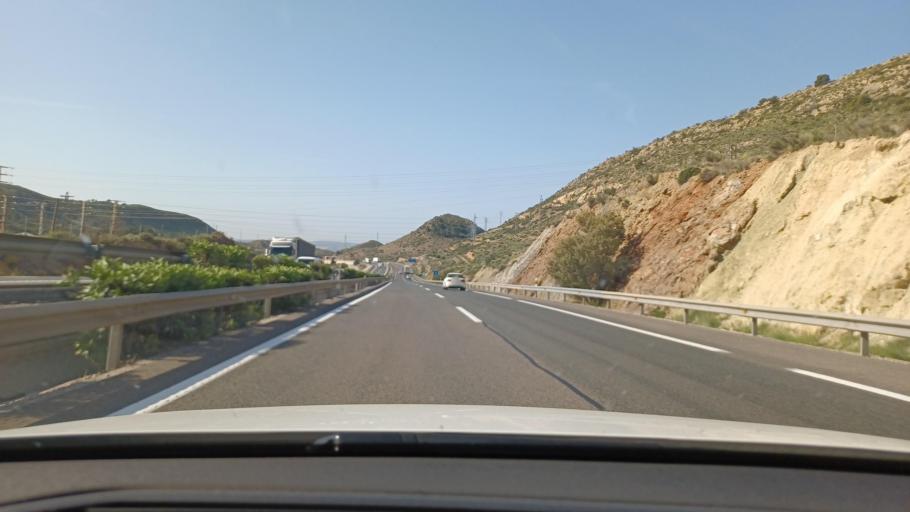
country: ES
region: Valencia
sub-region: Provincia de Alicante
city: Elda
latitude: 38.4399
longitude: -0.7832
